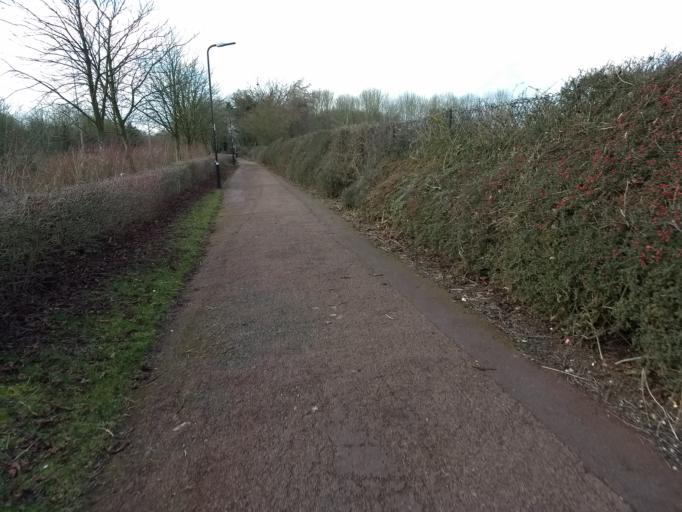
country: GB
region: England
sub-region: Milton Keynes
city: Milton Keynes
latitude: 52.0398
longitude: -0.7401
